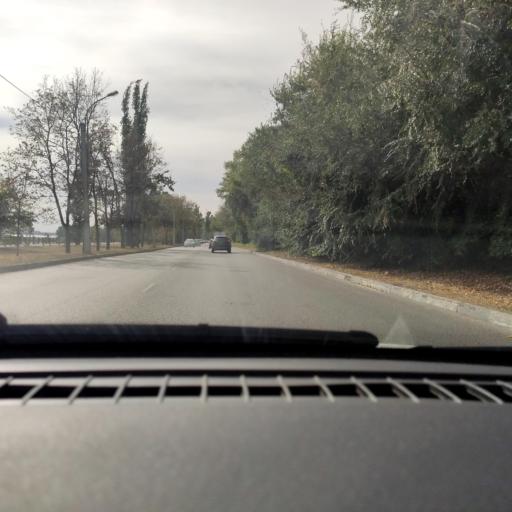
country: RU
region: Voronezj
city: Voronezh
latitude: 51.6654
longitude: 39.2204
